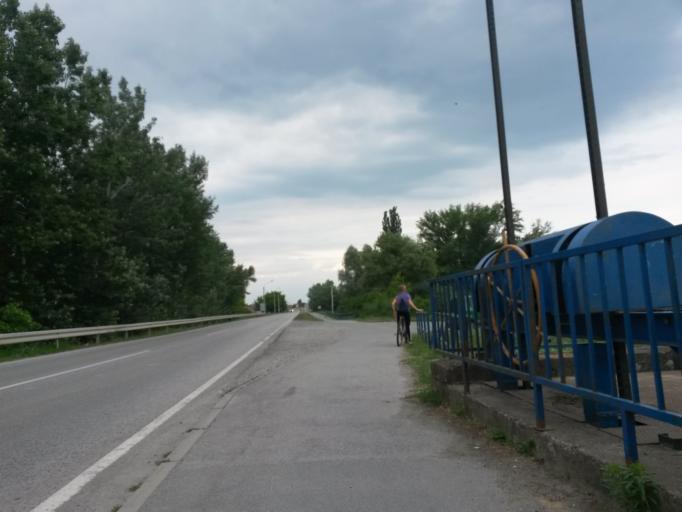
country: HR
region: Osjecko-Baranjska
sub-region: Grad Osijek
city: Bilje
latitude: 45.5909
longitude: 18.7362
